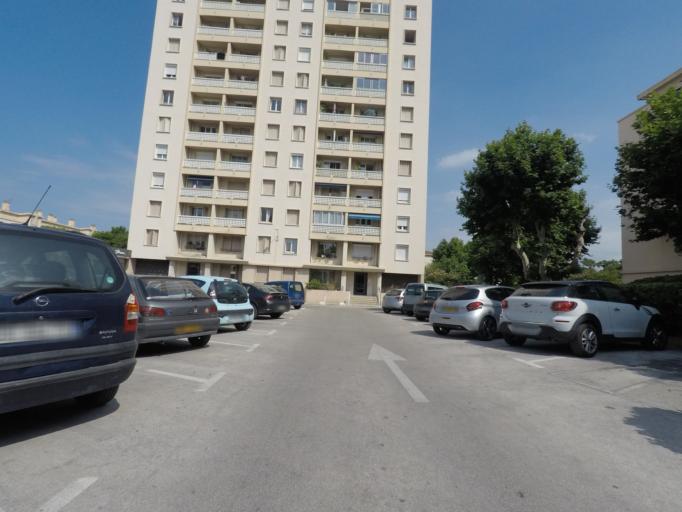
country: FR
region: Provence-Alpes-Cote d'Azur
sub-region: Departement des Bouches-du-Rhone
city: Marseille 10
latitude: 43.2685
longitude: 5.4121
